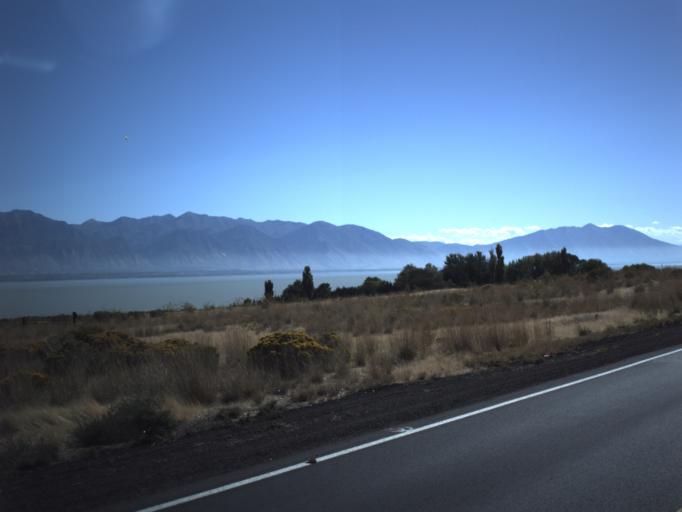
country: US
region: Utah
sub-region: Utah County
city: Saratoga Springs
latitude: 40.3057
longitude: -111.8869
